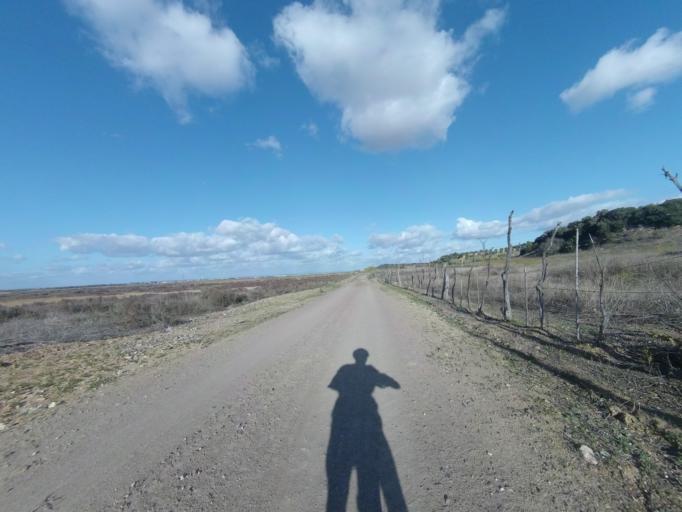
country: ES
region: Andalusia
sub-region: Provincia de Huelva
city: Moguer
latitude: 37.2621
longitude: -6.8702
